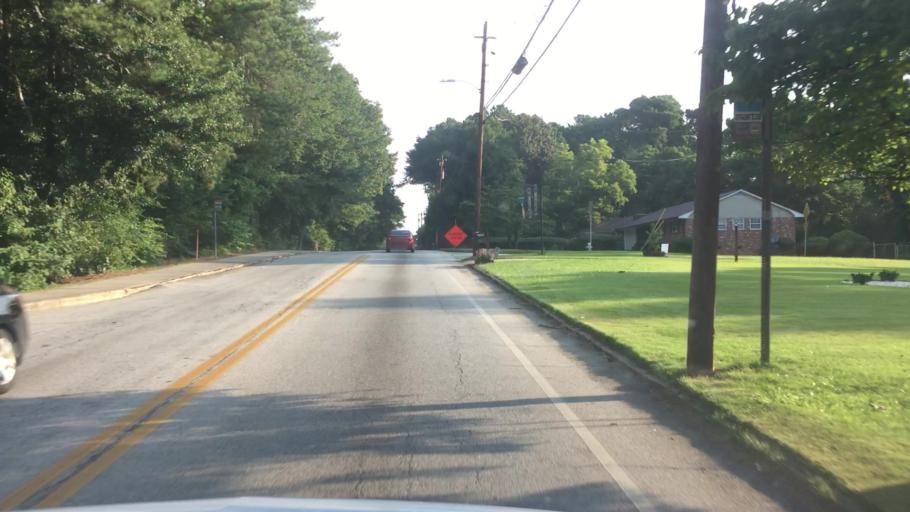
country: US
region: Georgia
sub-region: DeKalb County
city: Panthersville
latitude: 33.7081
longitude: -84.2525
